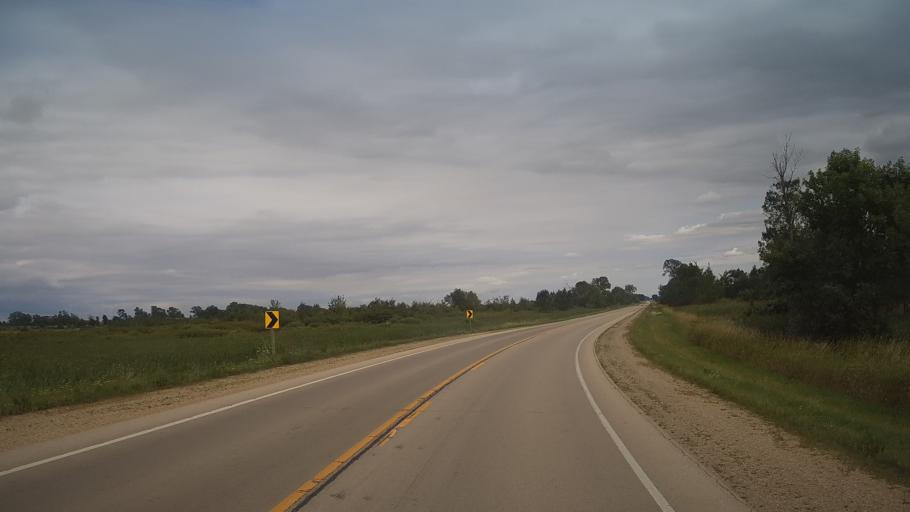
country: US
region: Wisconsin
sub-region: Green Lake County
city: Berlin
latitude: 44.0487
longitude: -88.9710
